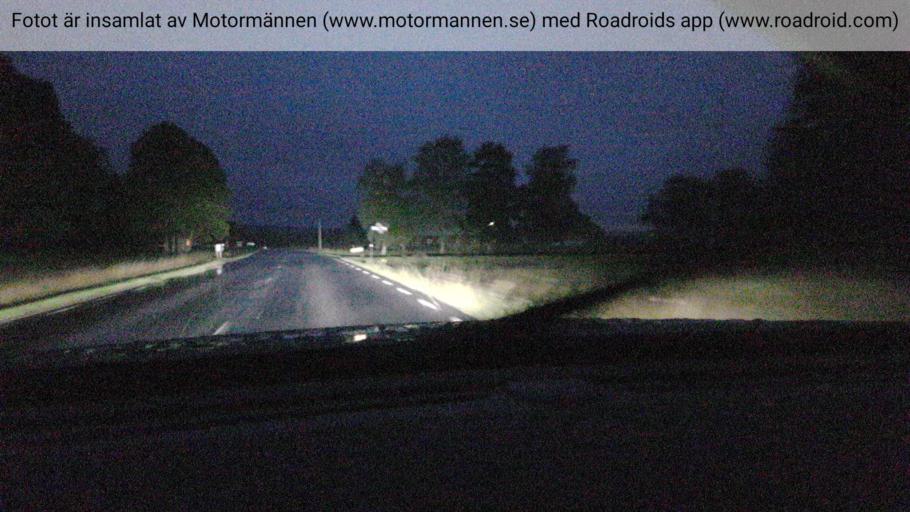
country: SE
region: Vaestra Goetaland
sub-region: Falkopings Kommun
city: Akarp
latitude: 58.3099
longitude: 13.7073
